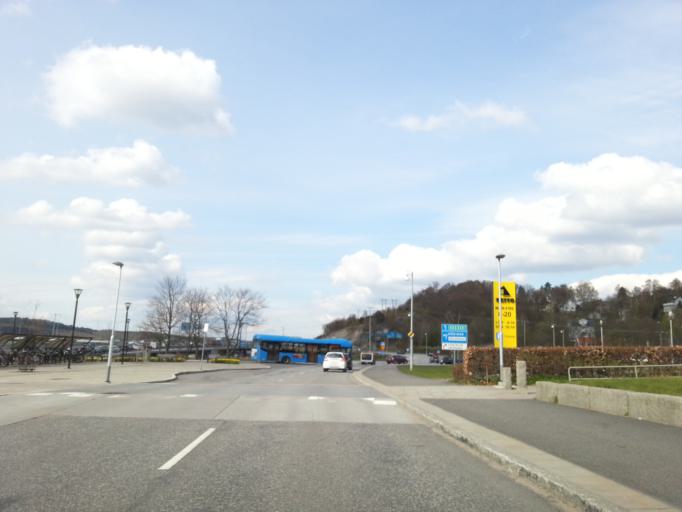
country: SE
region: Vaestra Goetaland
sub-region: Ale Kommun
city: Surte
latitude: 57.8515
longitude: 12.0153
